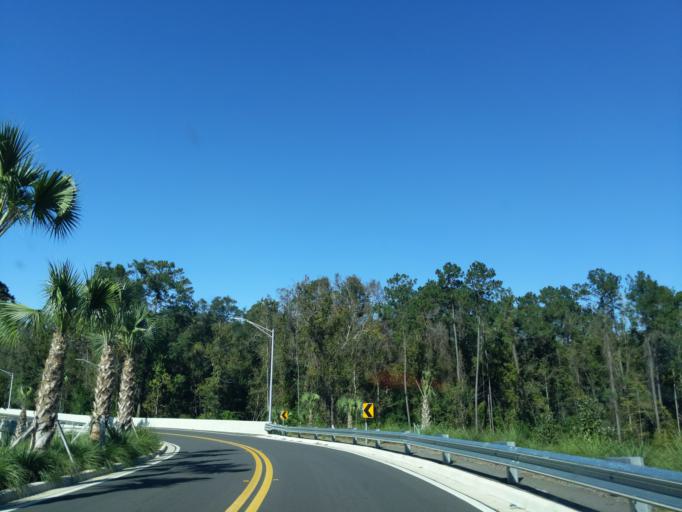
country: US
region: Florida
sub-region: Leon County
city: Tallahassee
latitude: 30.4634
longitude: -84.2229
